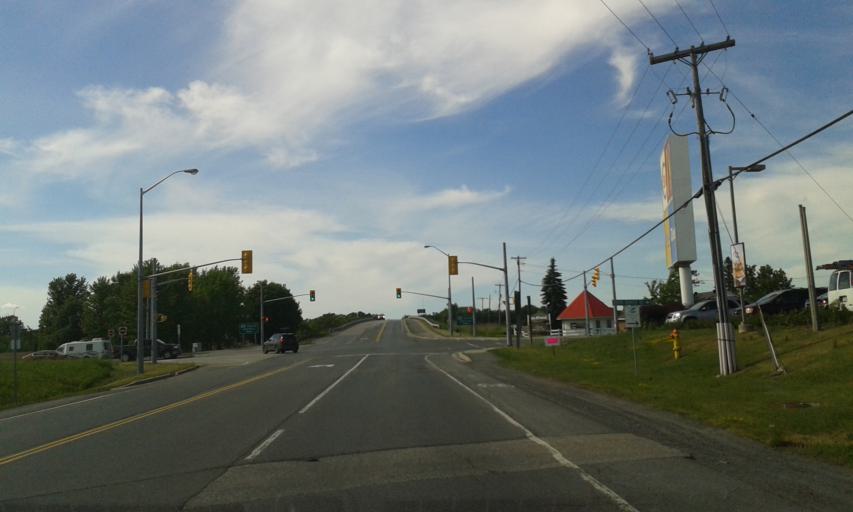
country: CA
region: Ontario
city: Cornwall
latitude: 45.1340
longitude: -74.4945
